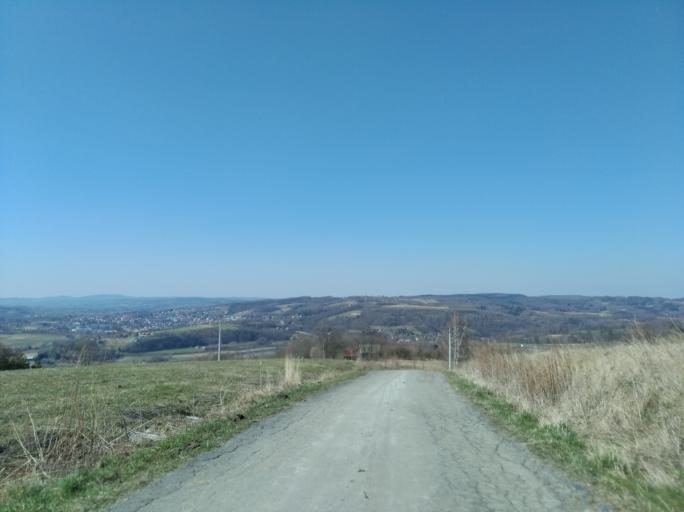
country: PL
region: Subcarpathian Voivodeship
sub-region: Powiat strzyzowski
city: Strzyzow
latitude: 49.8656
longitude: 21.8375
